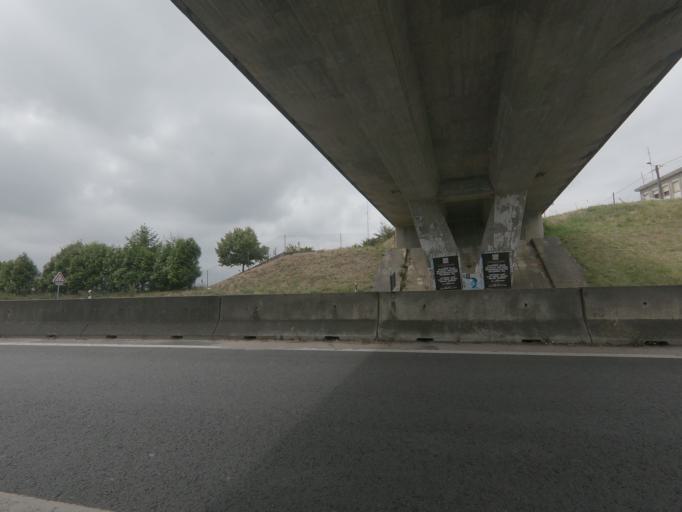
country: PT
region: Viana do Castelo
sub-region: Valenca
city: Valenca
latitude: 42.0260
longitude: -8.6469
